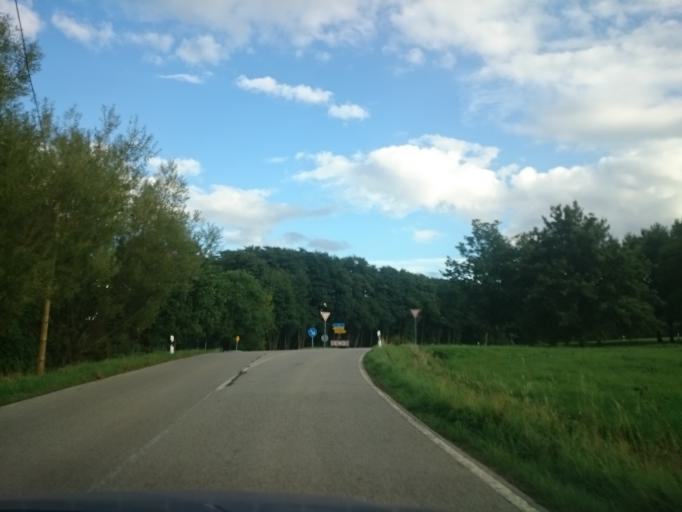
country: DE
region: Bavaria
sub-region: Regierungsbezirk Mittelfranken
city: Thalmassing
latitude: 49.1312
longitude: 11.1977
